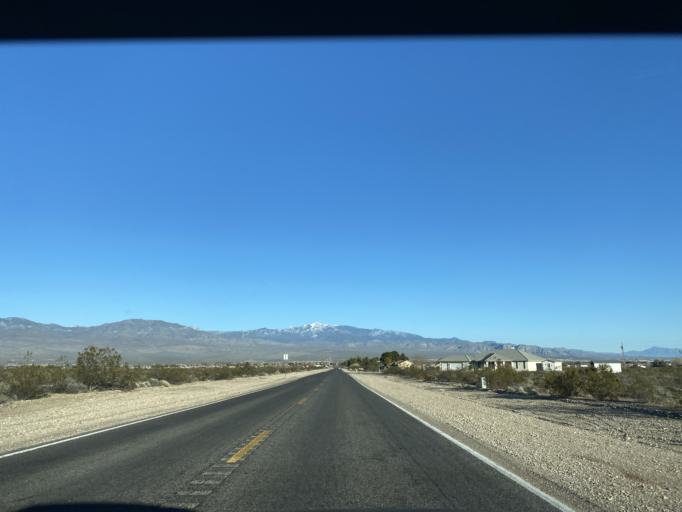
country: US
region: Nevada
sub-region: Nye County
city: Pahrump
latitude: 36.2636
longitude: -116.0942
